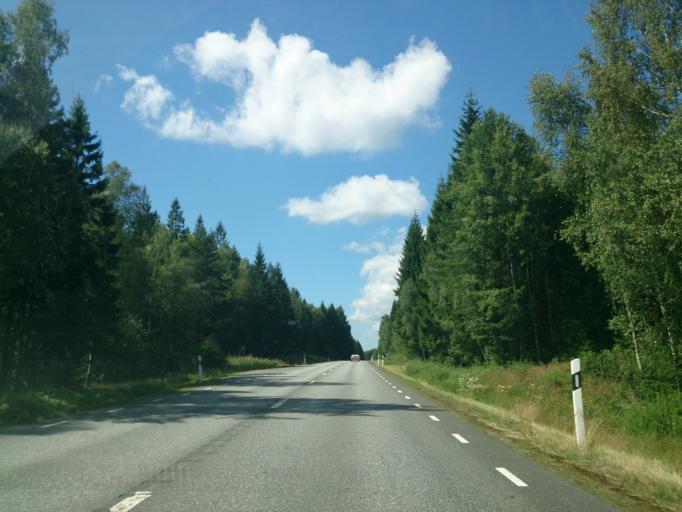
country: SE
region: Halland
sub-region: Hylte Kommun
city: Torup
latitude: 57.1277
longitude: 13.1223
